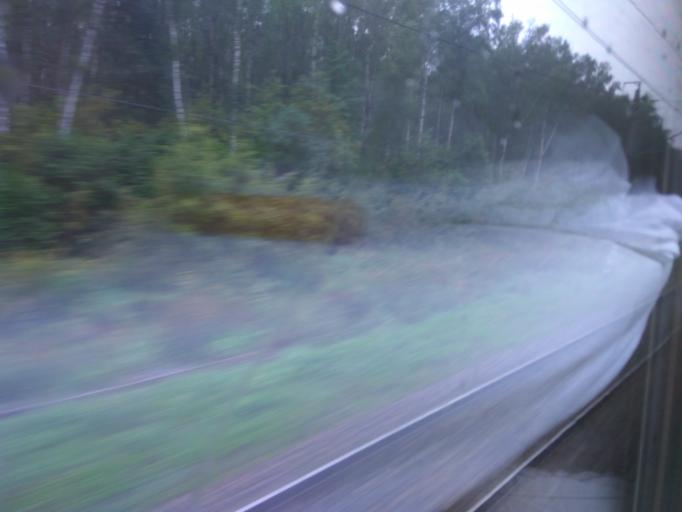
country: RU
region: Moskovskaya
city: Ozherel'ye
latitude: 54.8212
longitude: 38.2621
